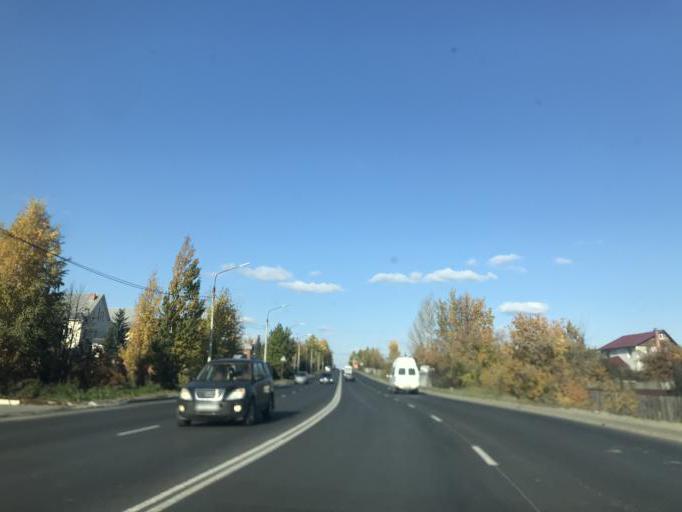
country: RU
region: Chelyabinsk
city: Roshchino
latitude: 55.2349
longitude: 61.3166
